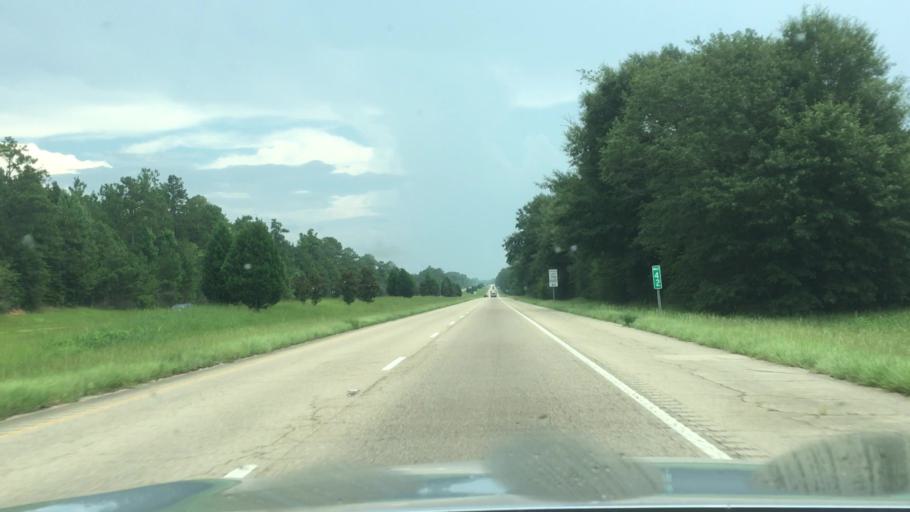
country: US
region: Mississippi
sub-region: Lamar County
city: Lumberton
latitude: 31.0075
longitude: -89.4151
